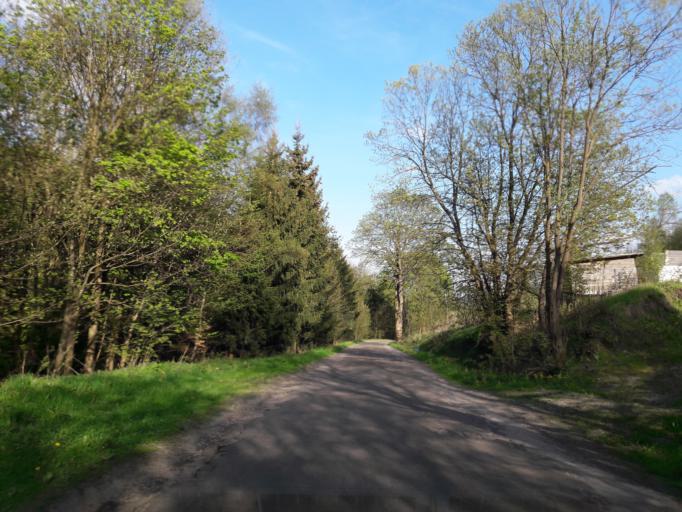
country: PL
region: Lower Silesian Voivodeship
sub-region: Powiat klodzki
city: Duszniki-Zdroj
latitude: 50.4431
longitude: 16.3435
